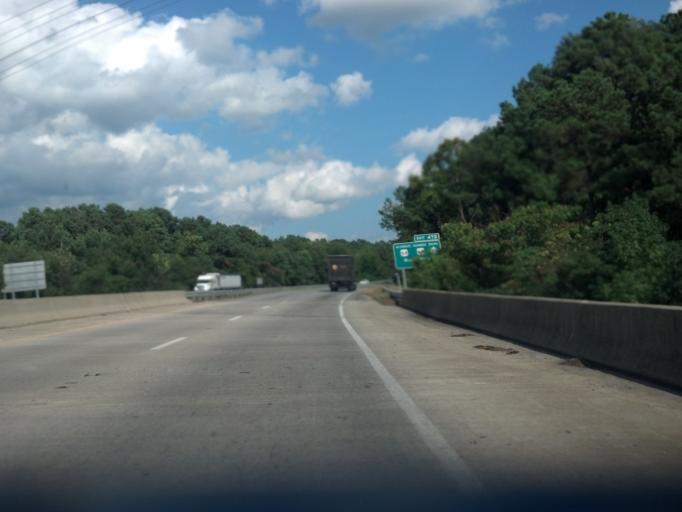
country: US
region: North Carolina
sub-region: Nash County
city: Rocky Mount
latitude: 35.9589
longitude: -77.7731
